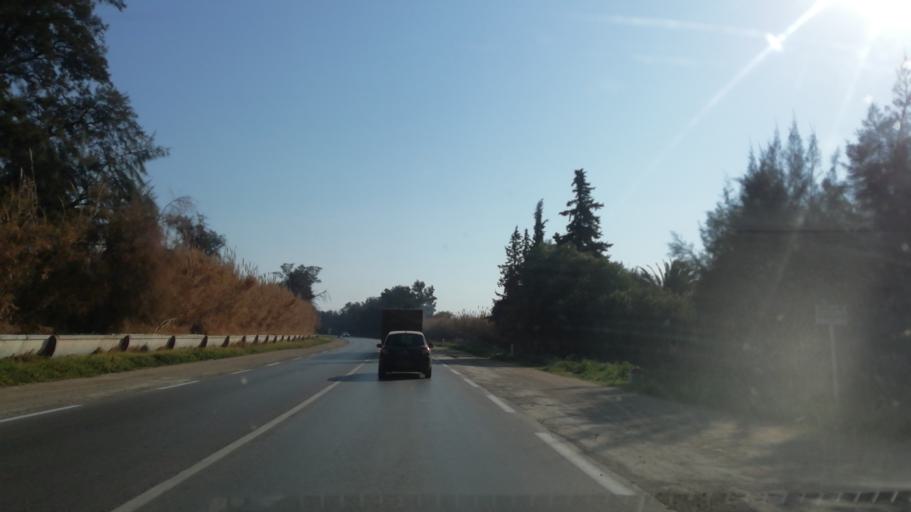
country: DZ
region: Relizane
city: Relizane
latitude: 35.7239
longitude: 0.4834
